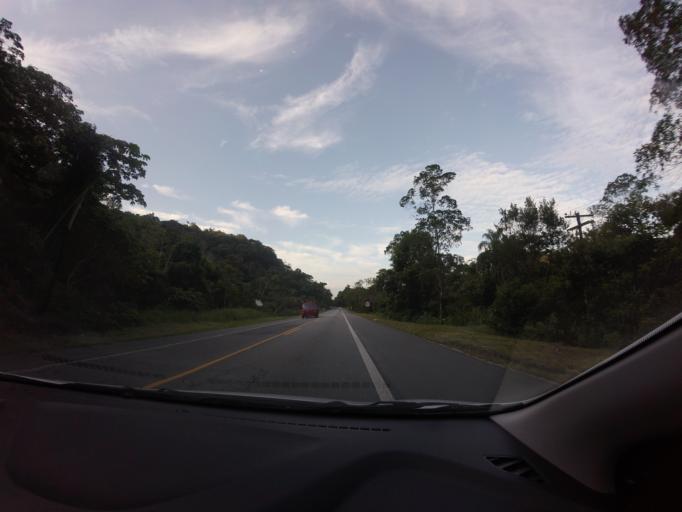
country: BR
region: Sao Paulo
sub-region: Bertioga
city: Bertioga
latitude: -23.8679
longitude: -46.1706
